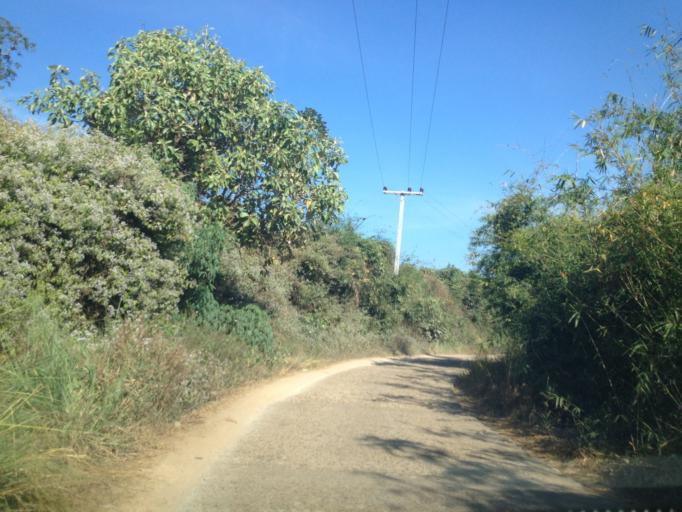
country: TH
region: Mae Hong Son
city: Ban Huai I Huak
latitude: 18.0506
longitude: 98.1673
